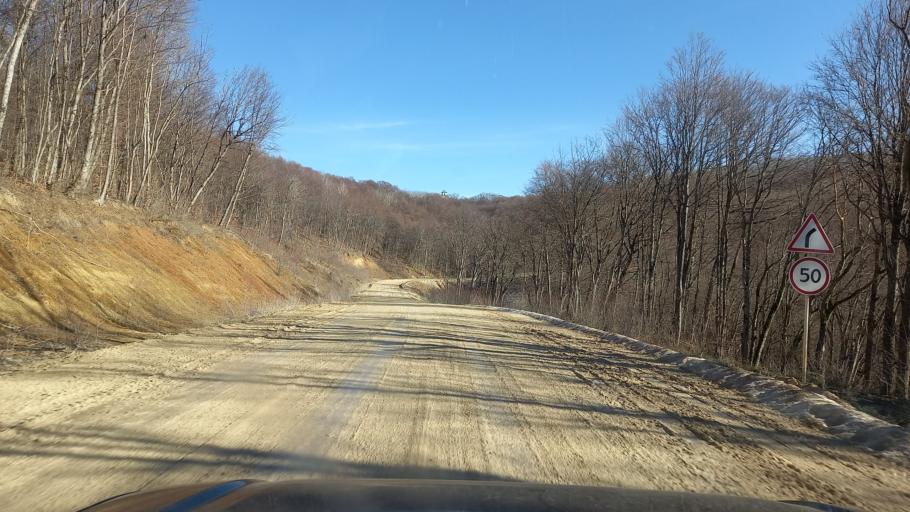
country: RU
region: Adygeya
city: Kamennomostskiy
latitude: 44.2876
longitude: 40.3069
